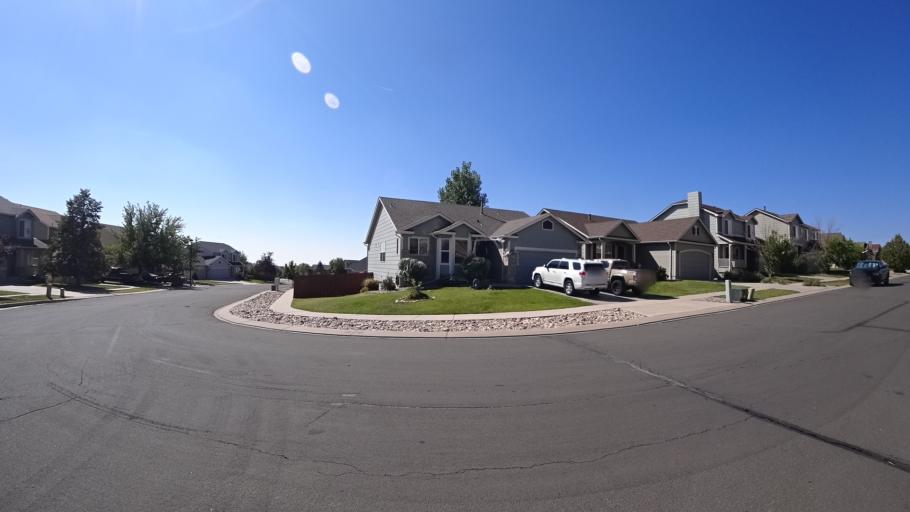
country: US
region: Colorado
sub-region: El Paso County
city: Cimarron Hills
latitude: 38.8972
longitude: -104.6909
